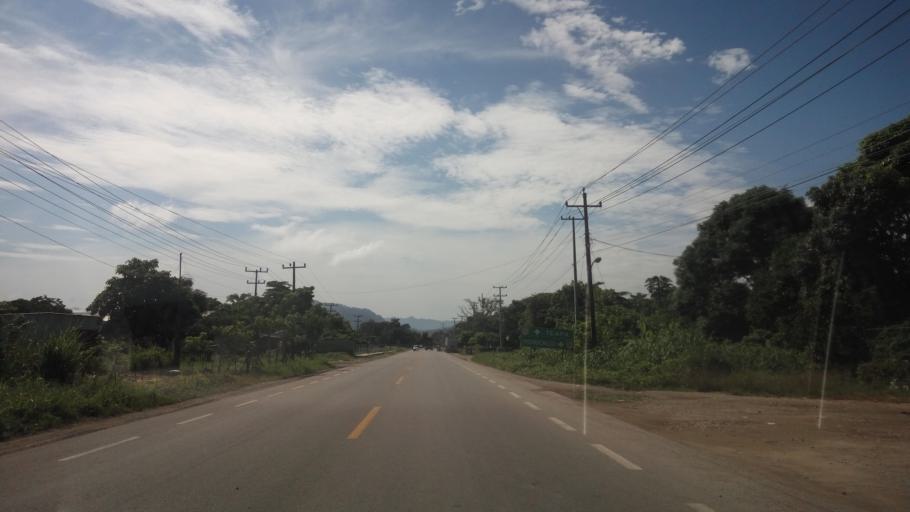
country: MX
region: Tabasco
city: Teapa
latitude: 17.5737
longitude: -92.9578
